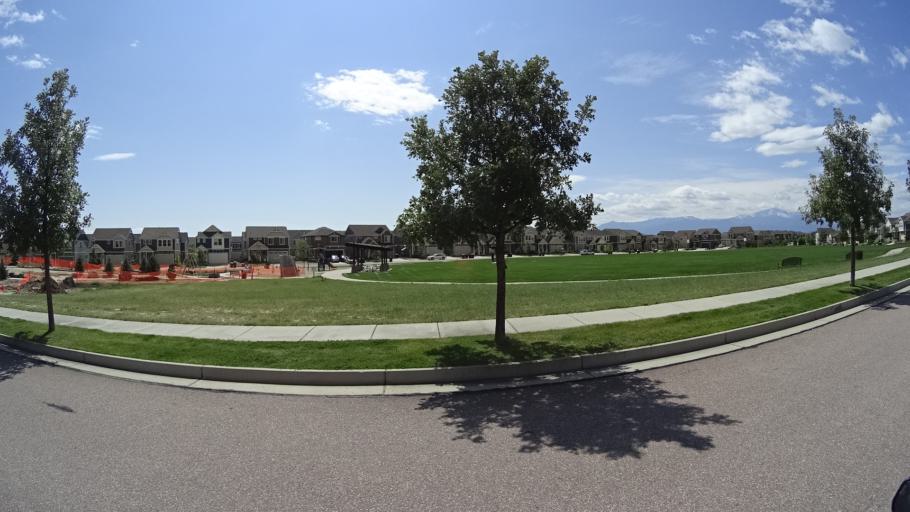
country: US
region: Colorado
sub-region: El Paso County
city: Cimarron Hills
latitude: 38.9286
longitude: -104.6722
